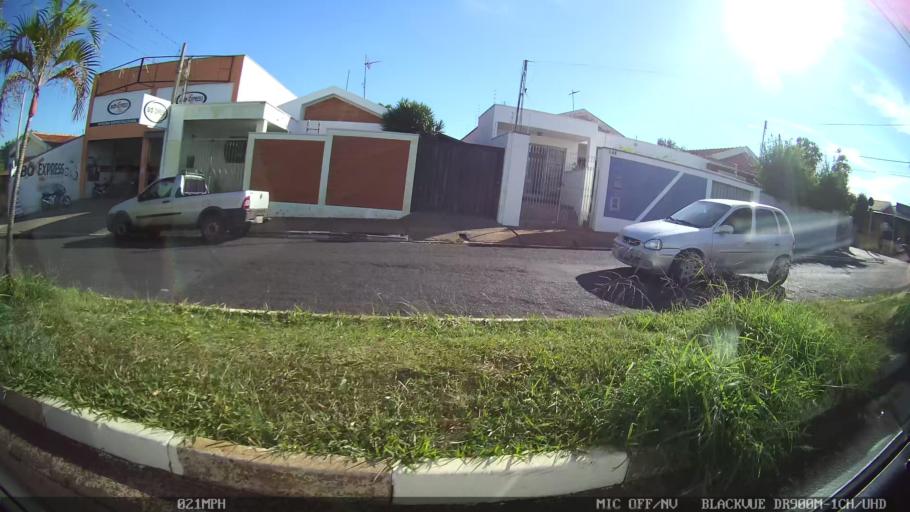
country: BR
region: Sao Paulo
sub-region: Araraquara
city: Araraquara
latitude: -21.7890
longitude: -48.1573
